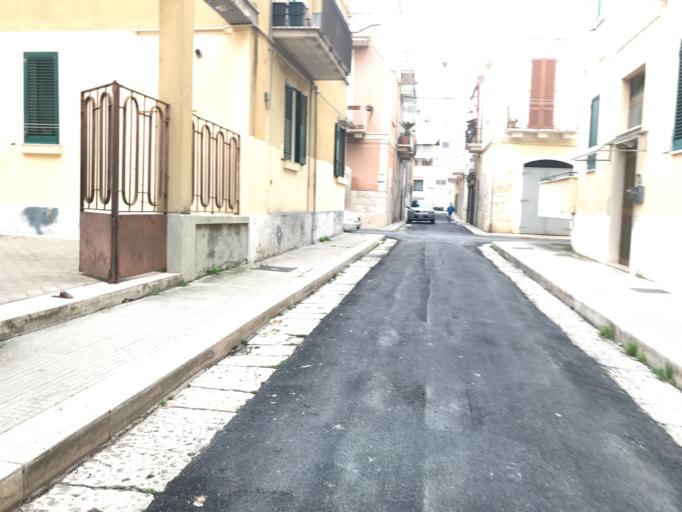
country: IT
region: Apulia
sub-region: Provincia di Bari
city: Corato
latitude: 41.1587
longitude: 16.4123
